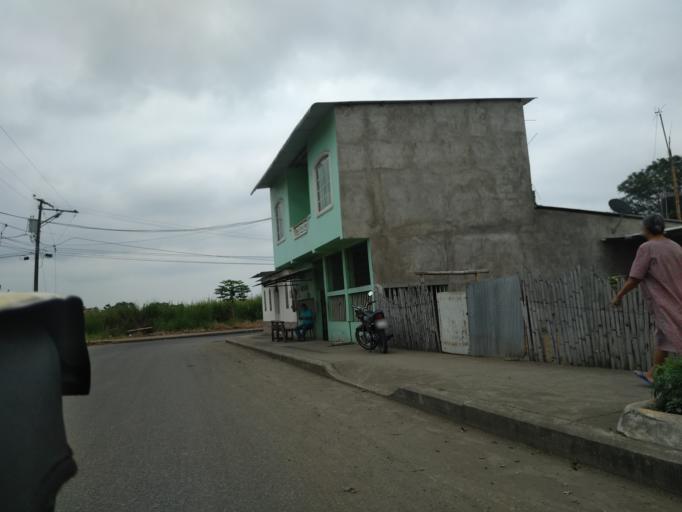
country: EC
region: Los Rios
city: Quevedo
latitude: -1.0254
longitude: -79.4416
